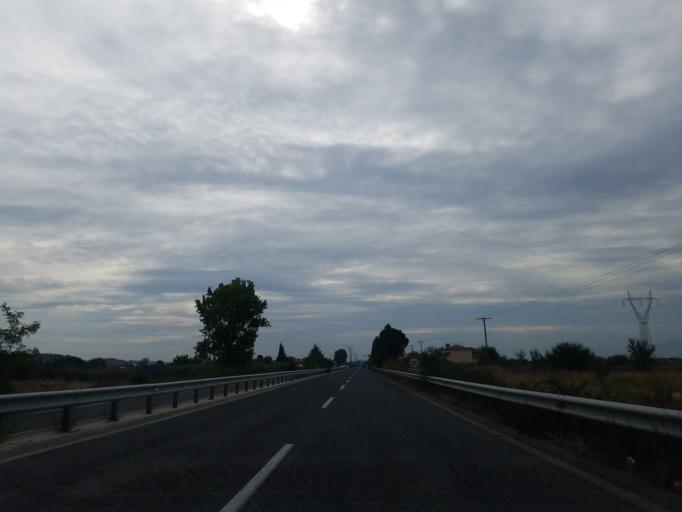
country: GR
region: Thessaly
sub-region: Trikala
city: Vasiliki
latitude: 39.6381
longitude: 21.6961
